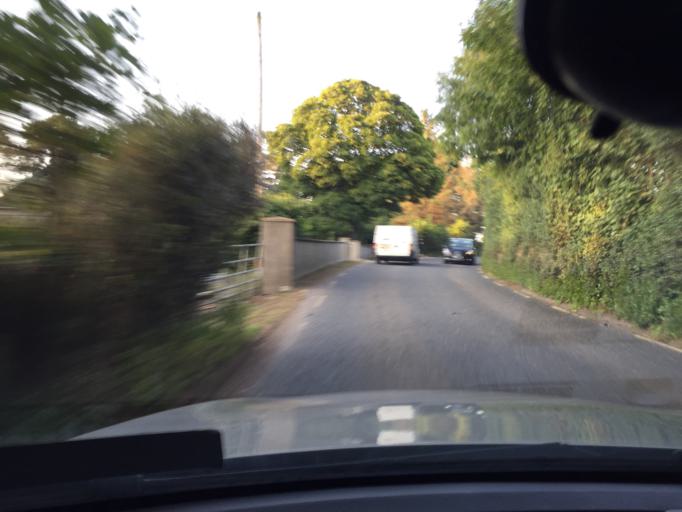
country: IE
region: Leinster
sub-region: Wicklow
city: Kilmacanoge
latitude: 53.1281
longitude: -6.1805
